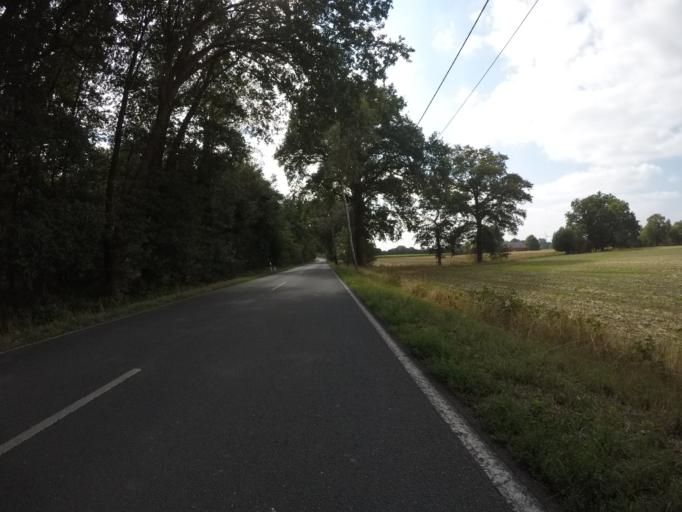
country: DE
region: North Rhine-Westphalia
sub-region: Regierungsbezirk Munster
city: Isselburg
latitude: 51.8111
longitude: 6.4779
